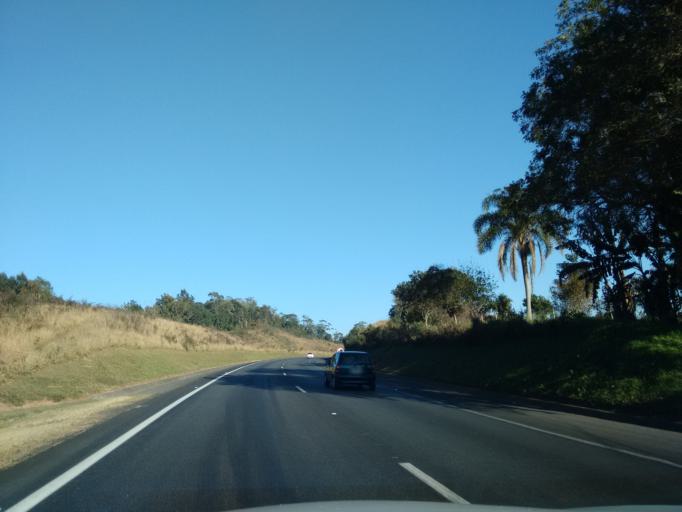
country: BR
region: Parana
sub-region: Campo Largo
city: Campo Largo
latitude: -25.4522
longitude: -49.5879
